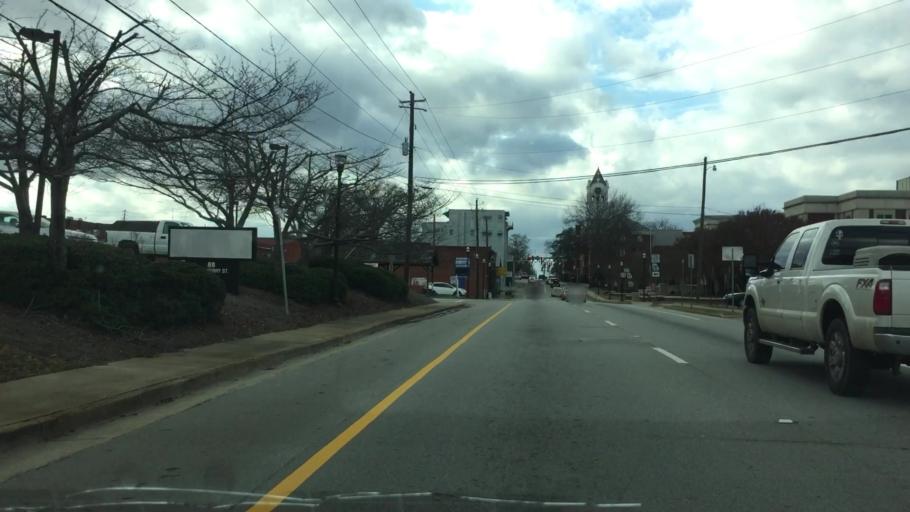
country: US
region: Georgia
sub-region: Henry County
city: McDonough
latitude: 33.4477
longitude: -84.1440
